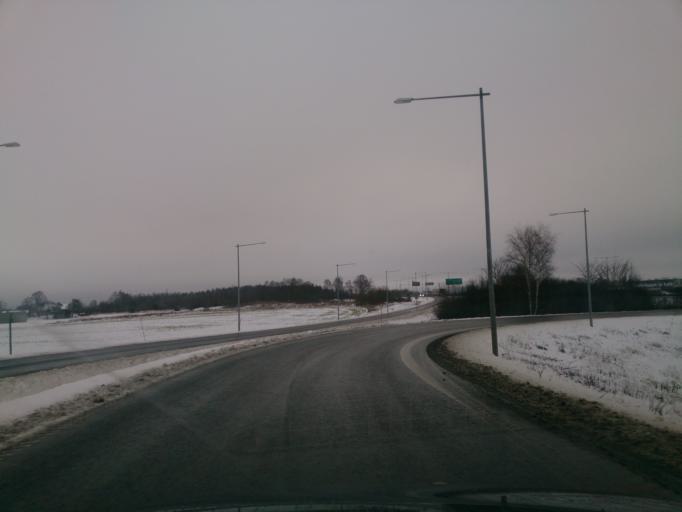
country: SE
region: OEstergoetland
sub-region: Norrkopings Kommun
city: Norrkoping
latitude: 58.6289
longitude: 16.1499
